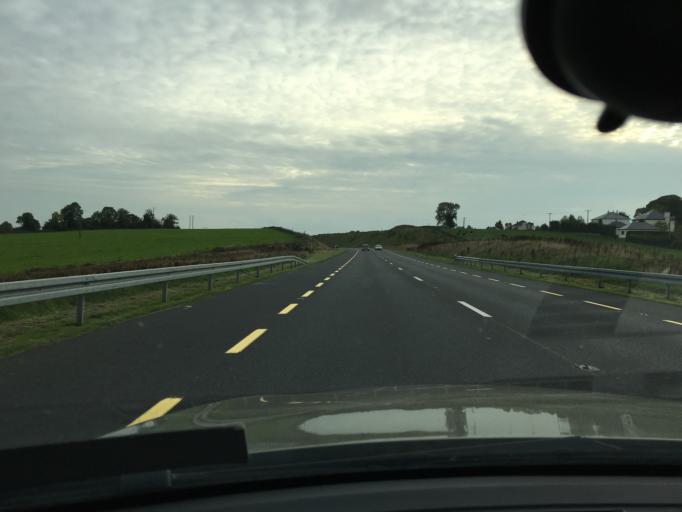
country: IE
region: Leinster
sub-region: An Longfort
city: Longford
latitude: 53.7322
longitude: -7.8223
